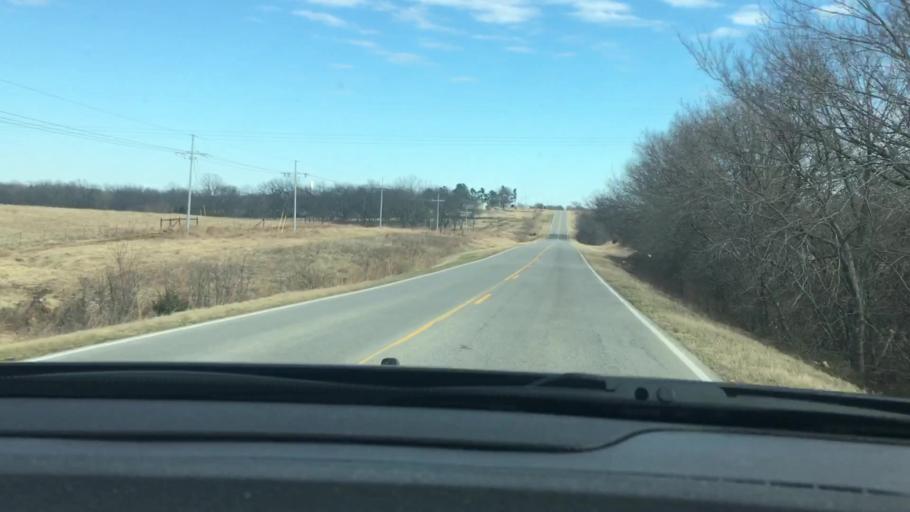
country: US
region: Oklahoma
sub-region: Garvin County
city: Stratford
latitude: 34.7968
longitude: -96.8281
